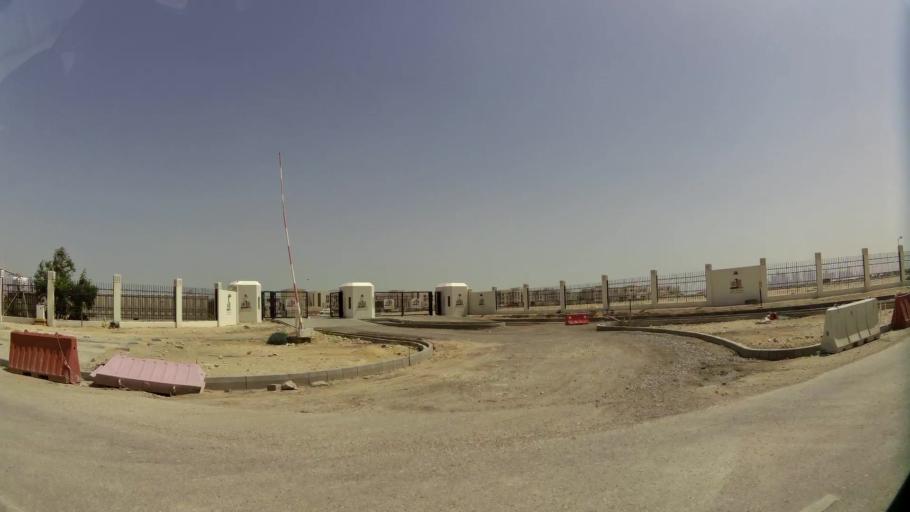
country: QA
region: Baladiyat Umm Salal
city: Umm Salal Muhammad
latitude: 25.3702
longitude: 51.4791
